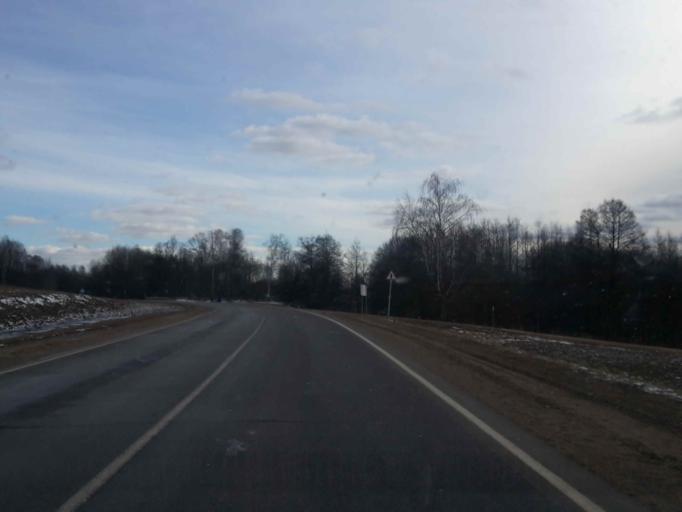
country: BY
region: Minsk
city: Myadzyel
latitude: 54.9895
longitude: 26.8869
